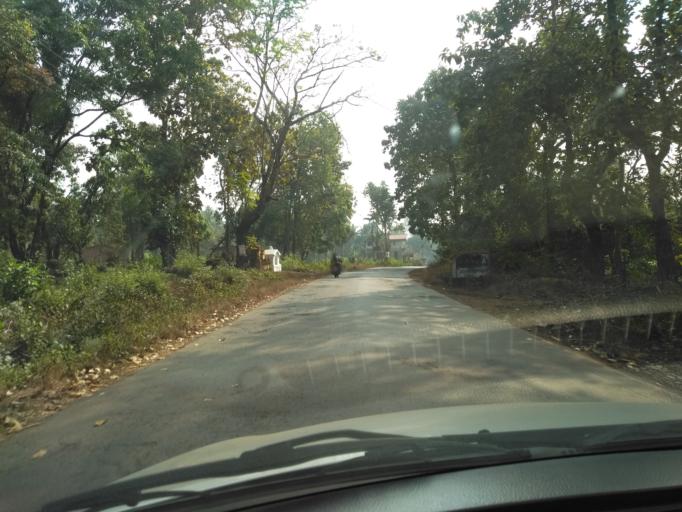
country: IN
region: Maharashtra
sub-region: Sindhudurg
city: Savantvadi
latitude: 15.8201
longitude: 73.8949
